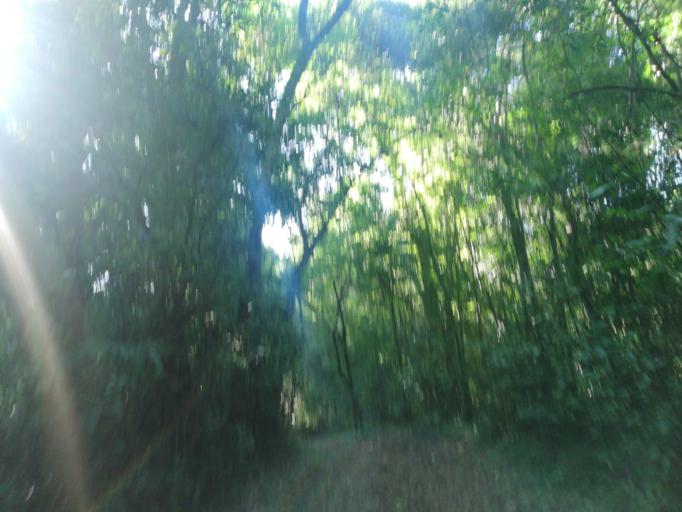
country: AR
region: Misiones
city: Cerro Azul
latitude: -27.7446
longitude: -55.5634
